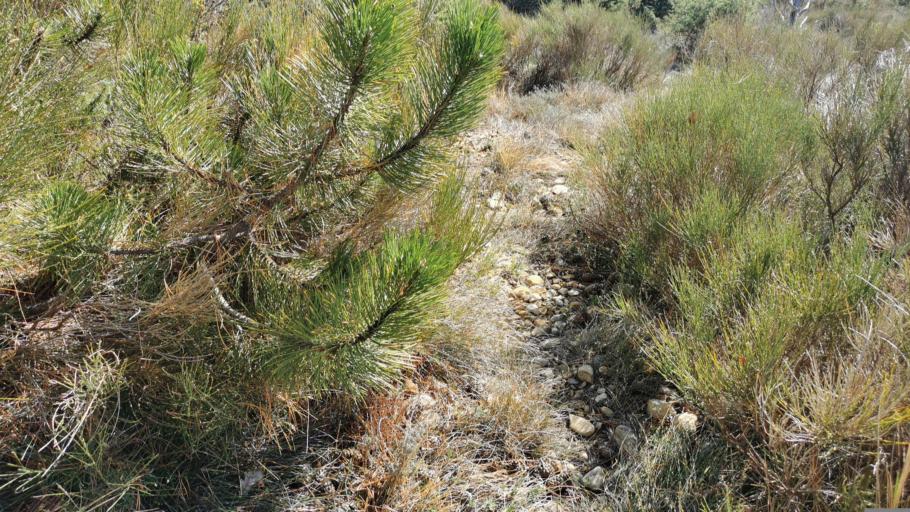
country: FR
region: Provence-Alpes-Cote d'Azur
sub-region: Departement des Alpes-de-Haute-Provence
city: Mallemoisson
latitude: 44.0660
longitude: 6.1250
